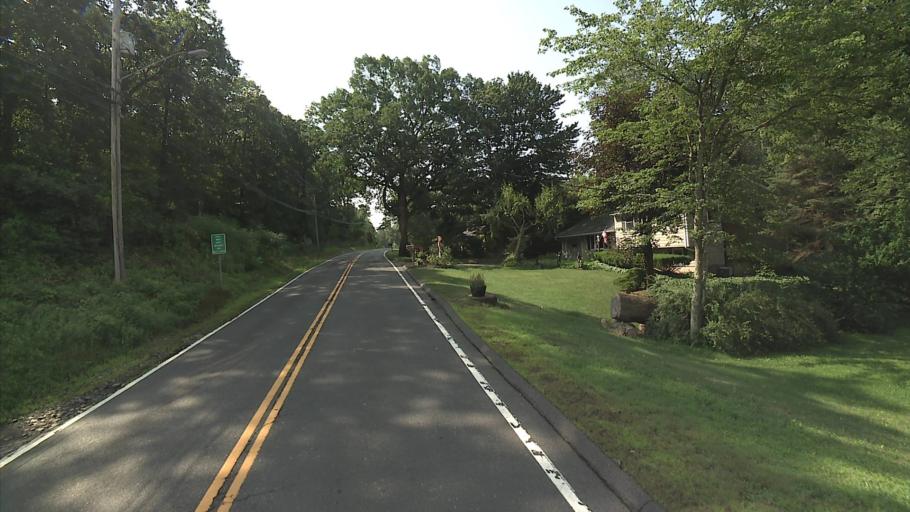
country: US
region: Connecticut
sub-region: New Haven County
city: Wolcott
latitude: 41.5943
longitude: -72.9587
